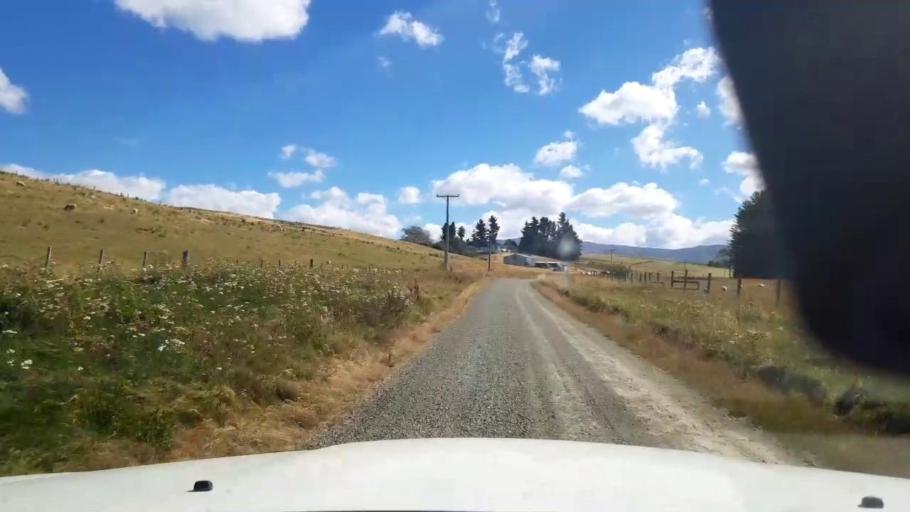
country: NZ
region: Canterbury
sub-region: Timaru District
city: Pleasant Point
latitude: -44.2374
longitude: 170.8678
